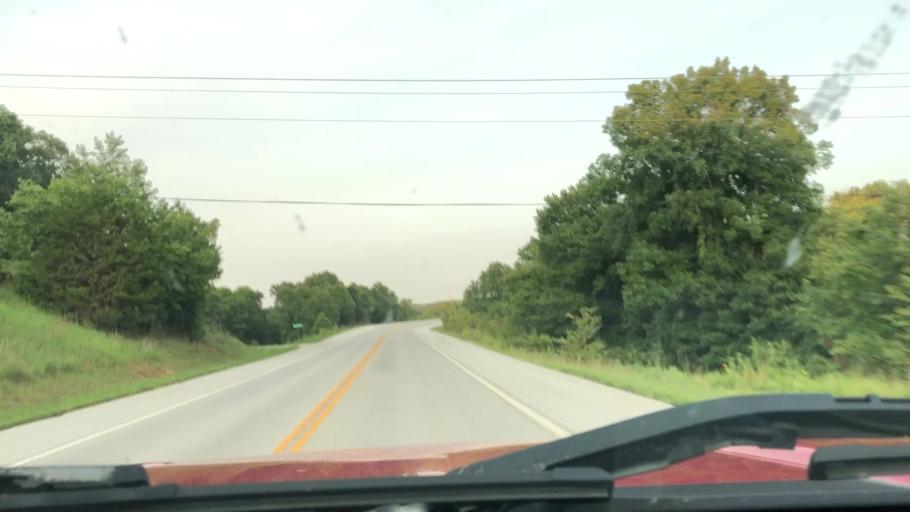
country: US
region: Missouri
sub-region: Jasper County
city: Duquesne
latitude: 36.9693
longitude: -94.4400
